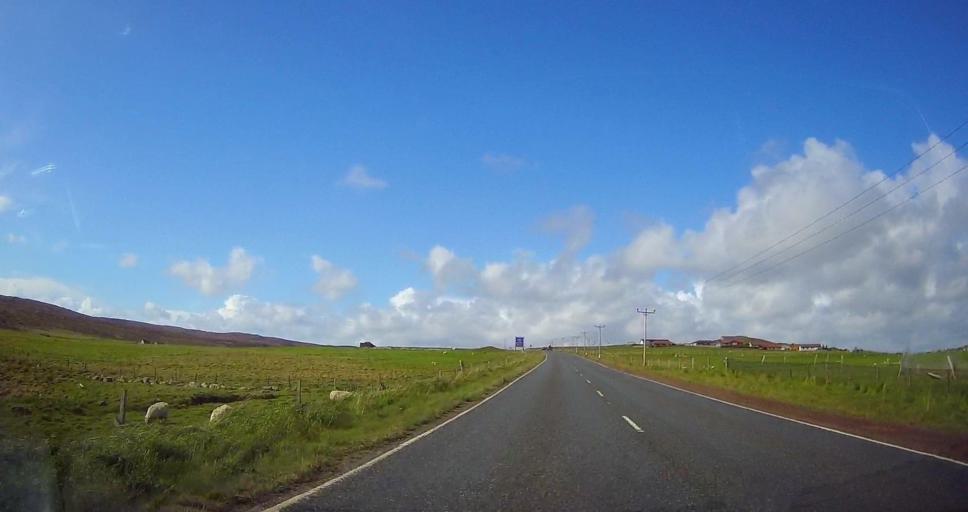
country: GB
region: Scotland
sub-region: Shetland Islands
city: Lerwick
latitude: 60.1948
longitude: -1.2321
